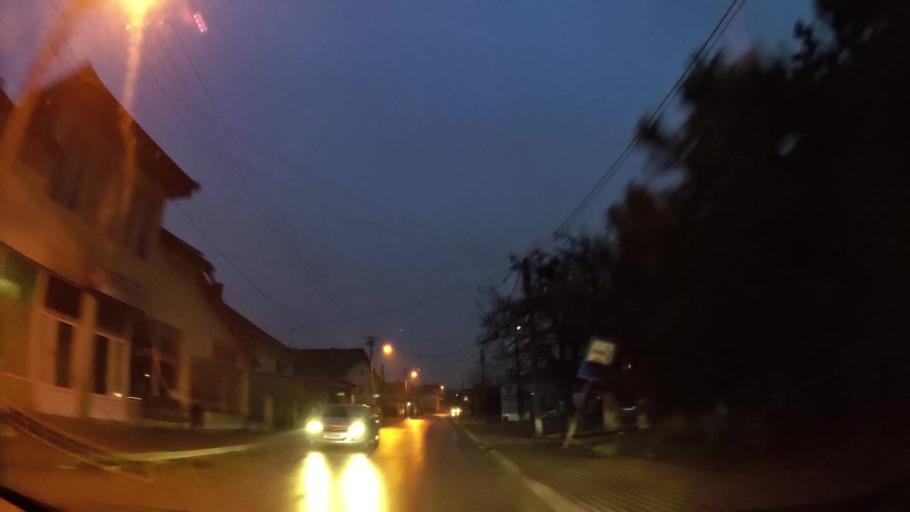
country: MK
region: Kisela Voda
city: Usje
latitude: 41.9709
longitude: 21.4826
